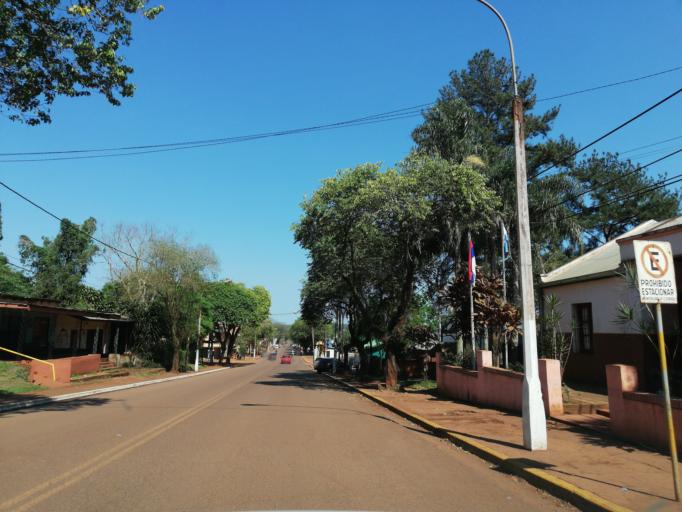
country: AR
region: Misiones
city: Puerto Eldorado
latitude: -26.4082
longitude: -54.6716
